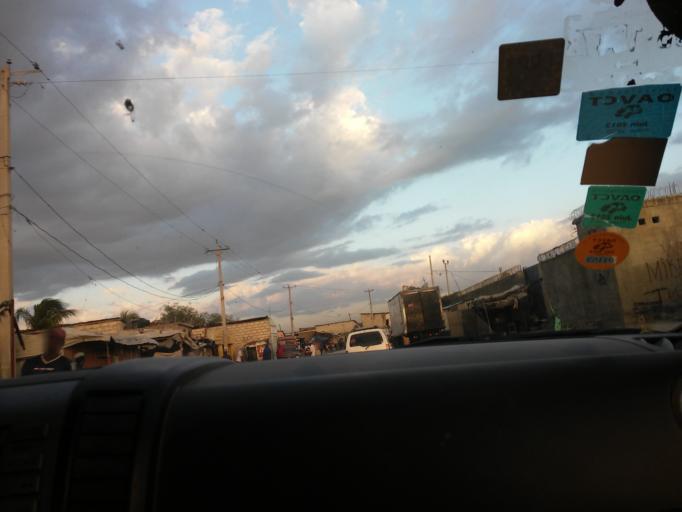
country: HT
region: Ouest
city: Port-au-Prince
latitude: 18.5654
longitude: -72.3472
